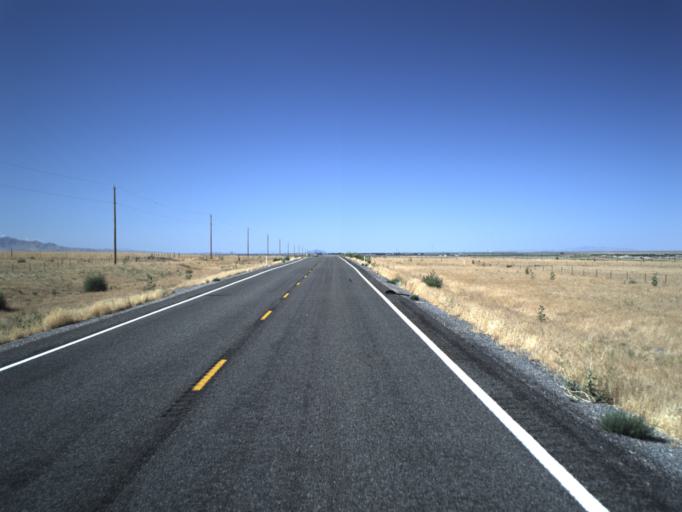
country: US
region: Utah
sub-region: Millard County
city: Delta
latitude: 39.6204
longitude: -112.3148
